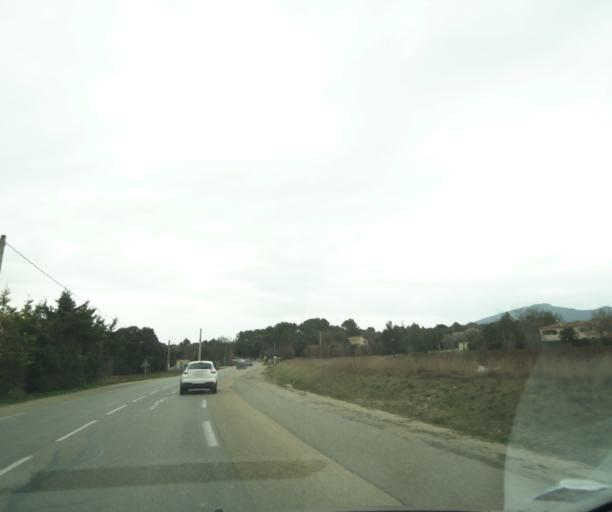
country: FR
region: Provence-Alpes-Cote d'Azur
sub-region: Departement des Bouches-du-Rhone
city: Jouques
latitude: 43.6402
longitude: 5.6147
